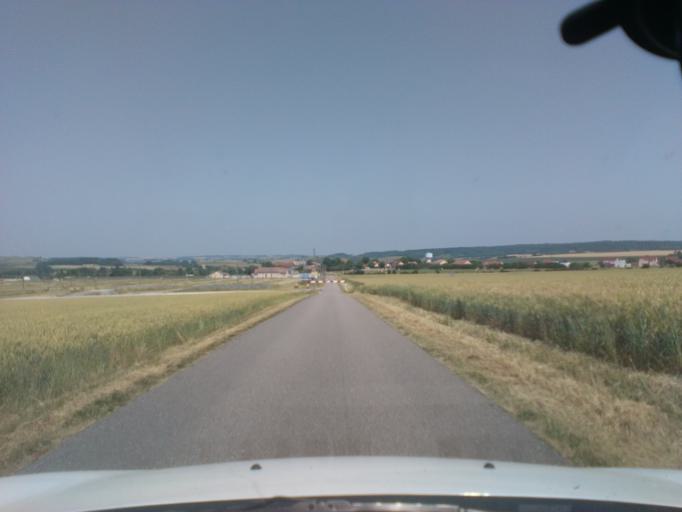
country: FR
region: Lorraine
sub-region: Departement des Vosges
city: Mirecourt
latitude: 48.3155
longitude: 6.1141
